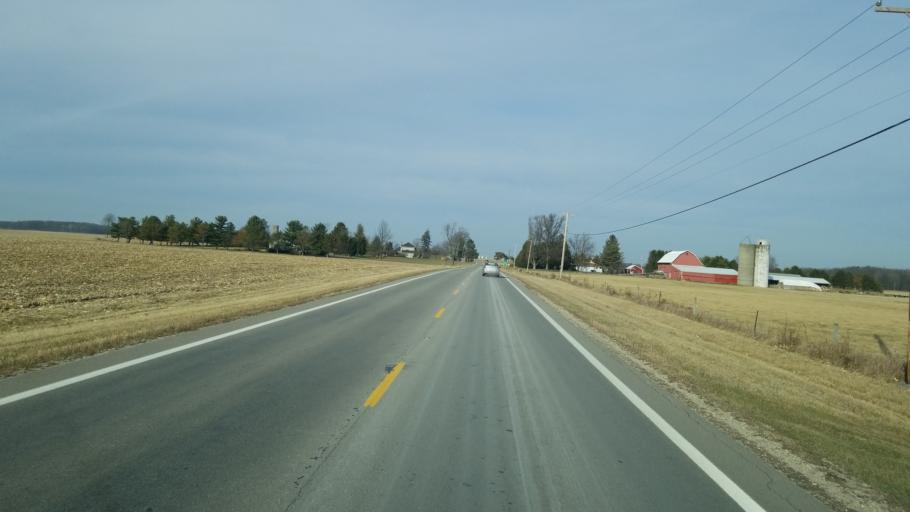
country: US
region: Ohio
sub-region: Union County
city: Marysville
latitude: 40.2761
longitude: -83.3758
